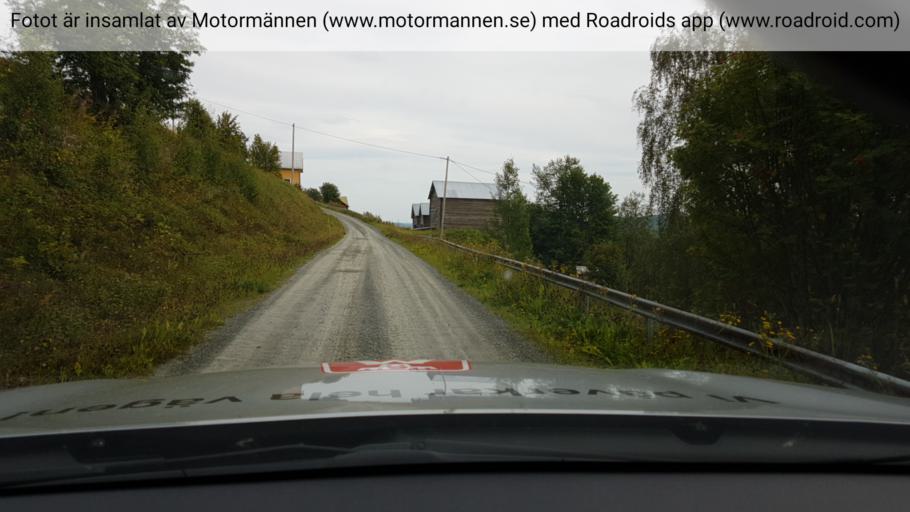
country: SE
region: Jaemtland
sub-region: Krokoms Kommun
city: Valla
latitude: 63.5827
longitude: 13.9853
